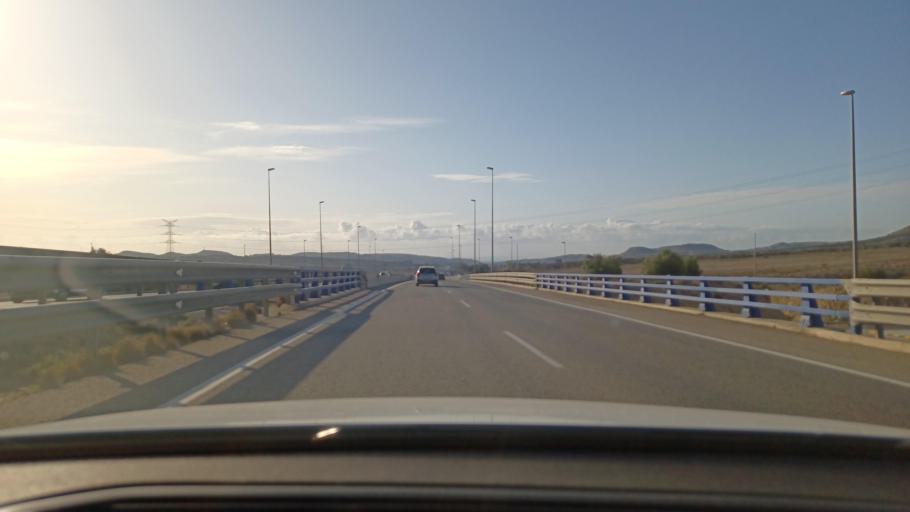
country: ES
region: Valencia
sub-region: Provincia de Alicante
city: Monforte del Cid
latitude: 38.3508
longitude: -0.6702
